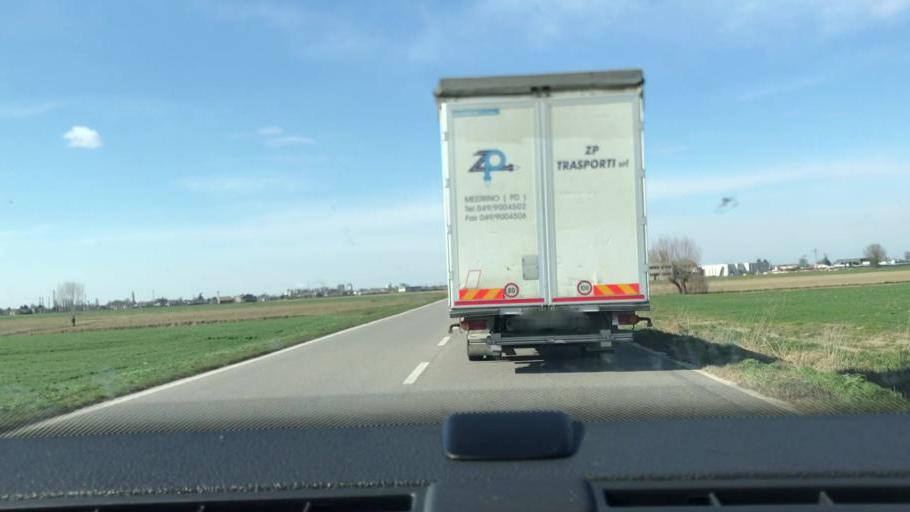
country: IT
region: Veneto
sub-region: Provincia di Rovigo
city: Calto
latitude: 45.0077
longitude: 11.3433
